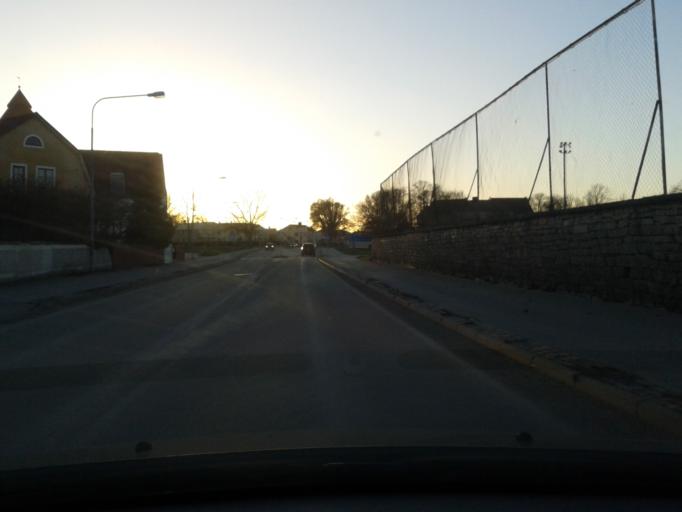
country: SE
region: Gotland
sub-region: Gotland
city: Visby
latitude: 57.6344
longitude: 18.2975
